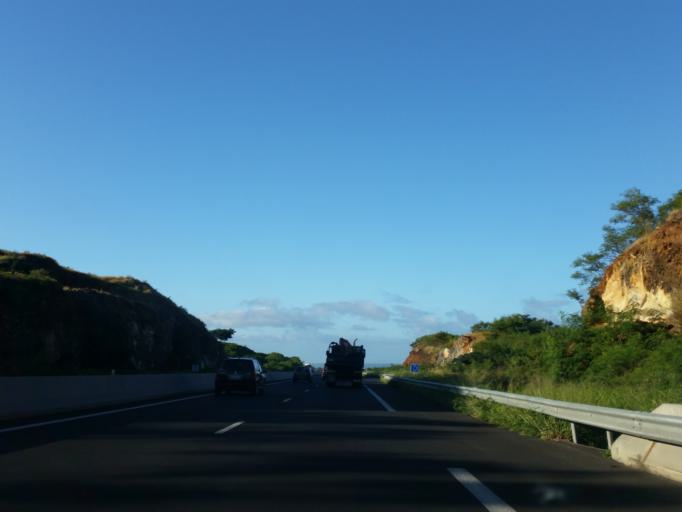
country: RE
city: Piton Saint-Leu
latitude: -21.2362
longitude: 55.3137
